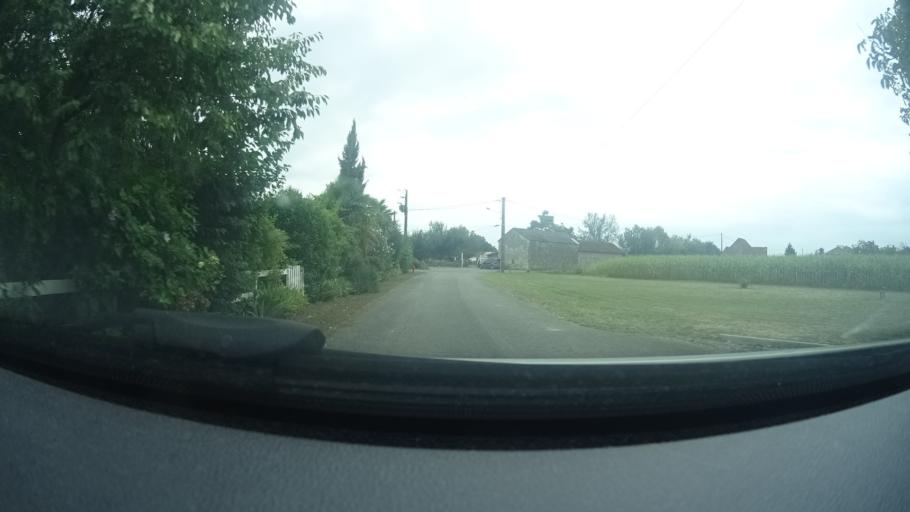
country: FR
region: Aquitaine
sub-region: Departement des Pyrenees-Atlantiques
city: Mont
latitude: 43.4531
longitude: -0.7117
